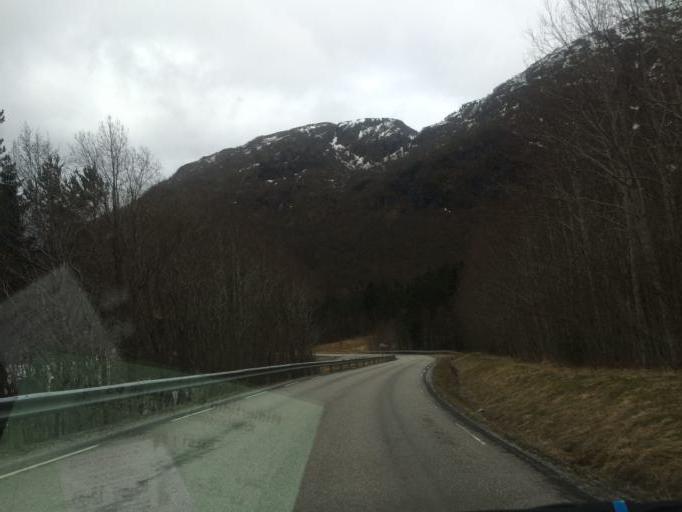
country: NO
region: More og Romsdal
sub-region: Gjemnes
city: Batnfjordsora
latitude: 62.9665
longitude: 7.7398
